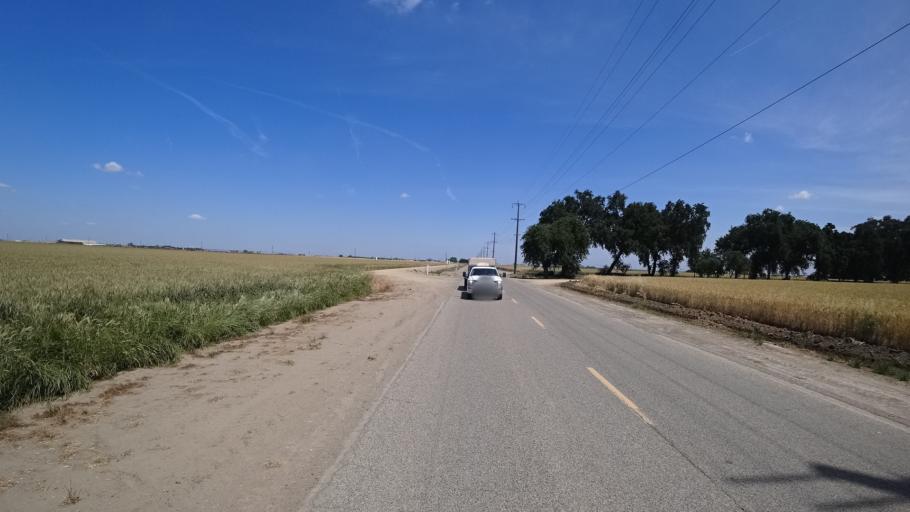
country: US
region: California
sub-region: Tulare County
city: Goshen
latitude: 36.2873
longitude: -119.4744
